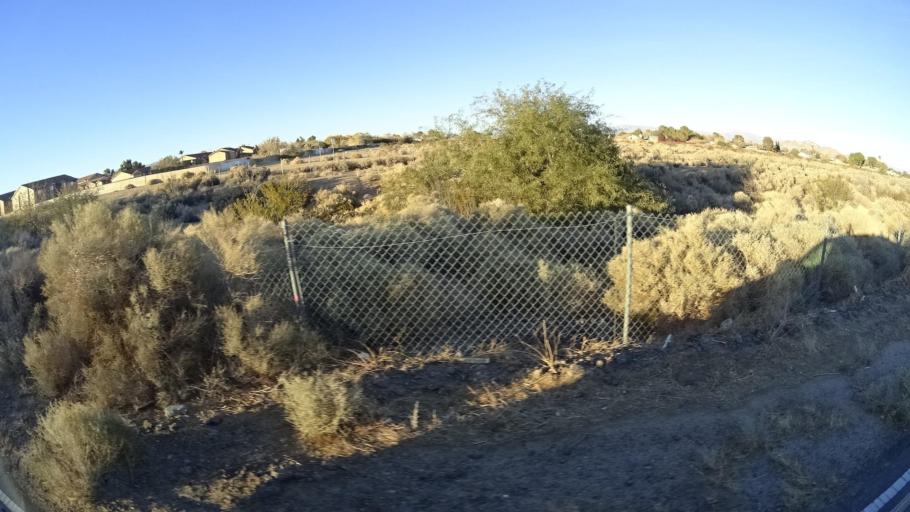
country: US
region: California
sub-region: Kern County
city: Ridgecrest
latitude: 35.6078
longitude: -117.6770
